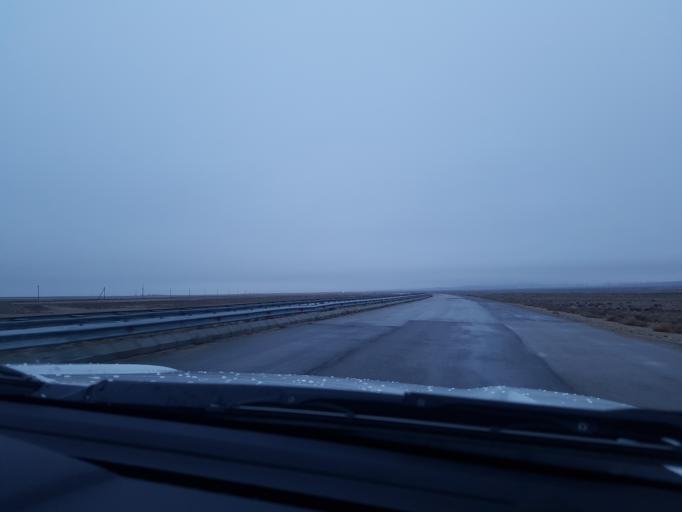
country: TM
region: Balkan
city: Balkanabat
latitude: 39.8810
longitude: 54.0552
